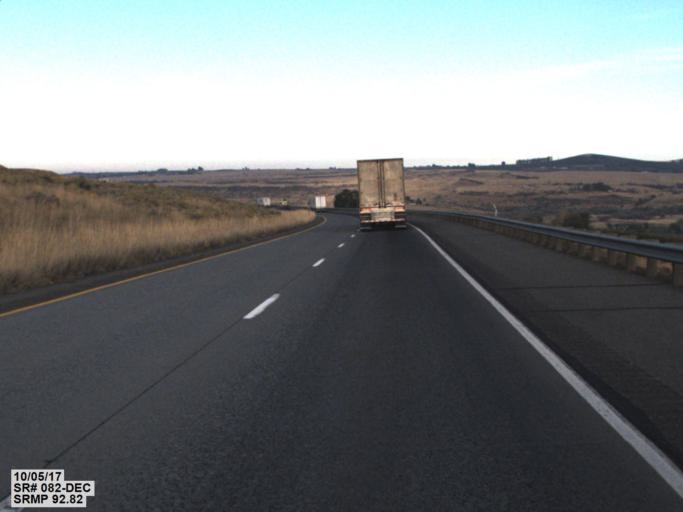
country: US
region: Washington
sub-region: Benton County
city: Benton City
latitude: 46.2674
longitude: -119.5507
